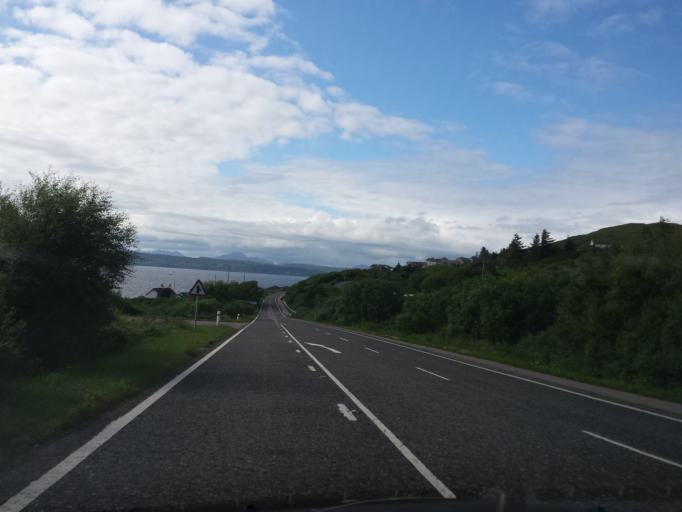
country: GB
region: Scotland
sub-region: Argyll and Bute
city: Isle Of Mull
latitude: 56.9910
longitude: -5.8274
